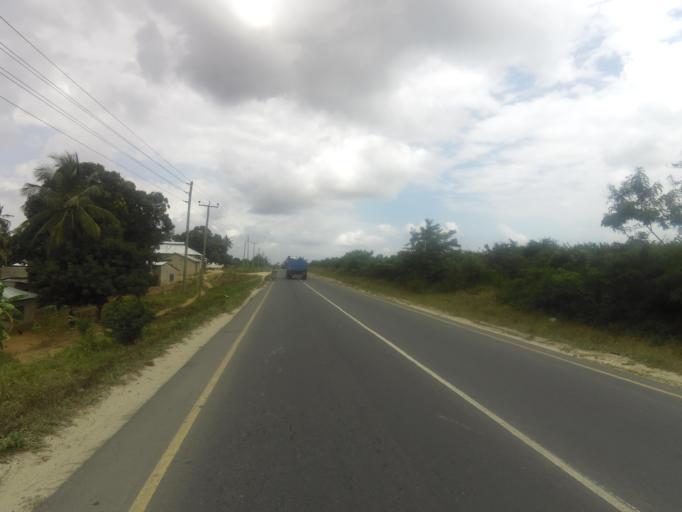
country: TZ
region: Pwani
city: Vikindu
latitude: -6.9696
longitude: 39.2857
